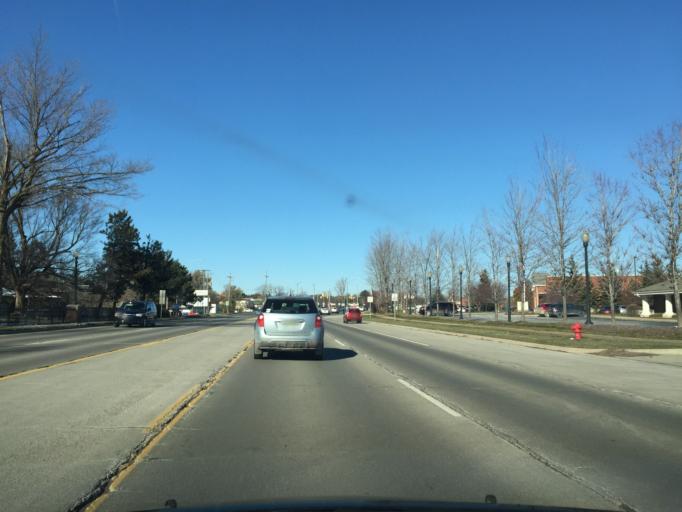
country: US
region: Michigan
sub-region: Oakland County
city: Lake Orion
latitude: 42.7874
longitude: -83.2447
